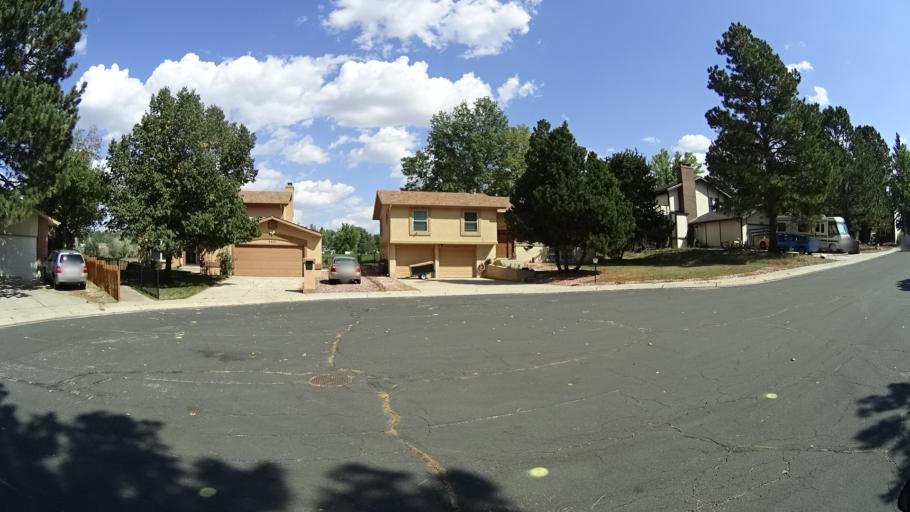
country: US
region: Colorado
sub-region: El Paso County
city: Cimarron Hills
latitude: 38.8763
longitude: -104.7471
